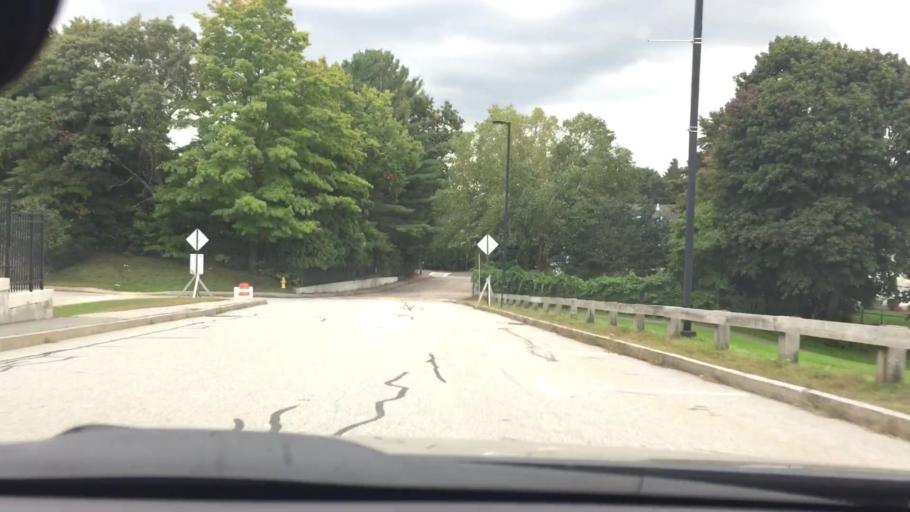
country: US
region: Massachusetts
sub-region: Norfolk County
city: Needham
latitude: 42.2858
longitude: -71.2321
